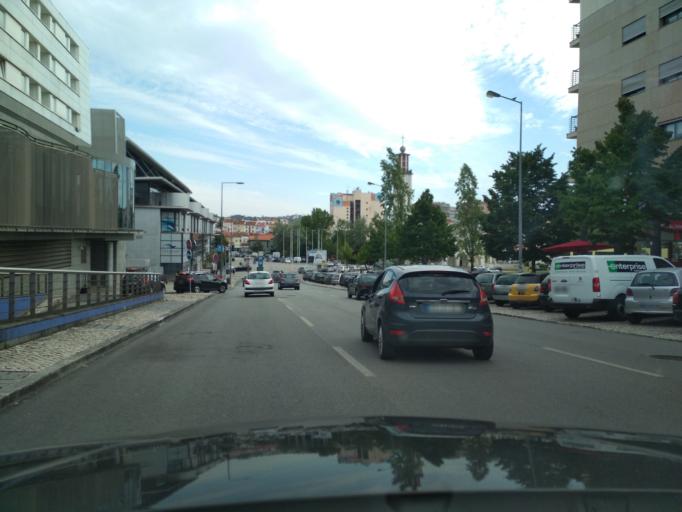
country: PT
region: Coimbra
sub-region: Coimbra
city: Coimbra
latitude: 40.2048
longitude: -8.4089
